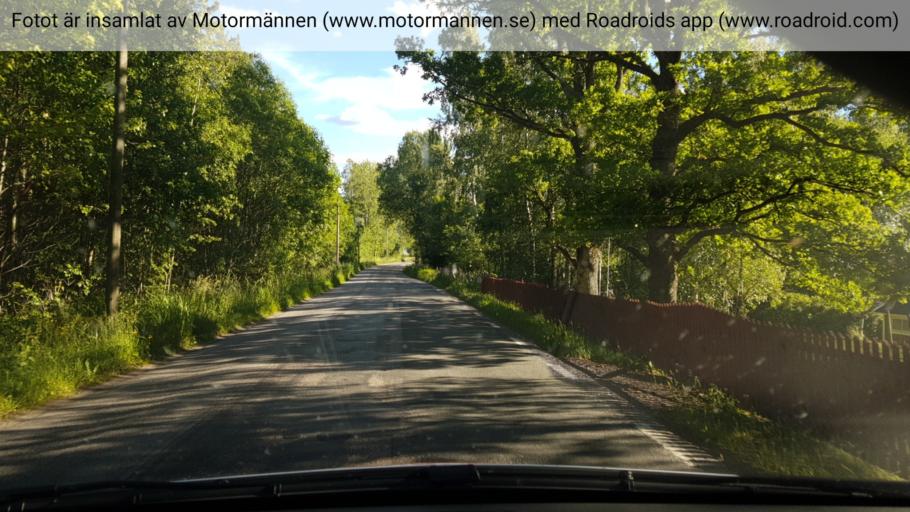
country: SE
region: Vaestra Goetaland
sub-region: Skovde Kommun
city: Stopen
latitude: 58.4853
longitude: 13.8667
